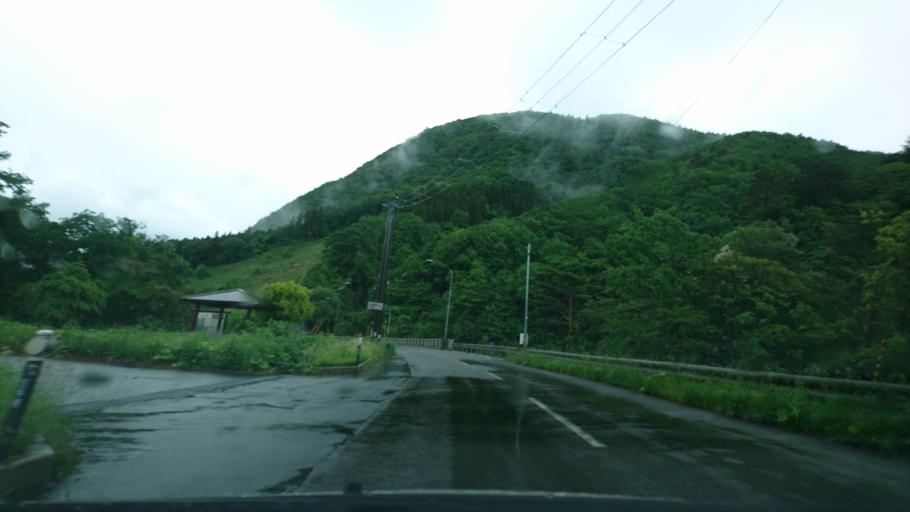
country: JP
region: Iwate
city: Ichinoseki
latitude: 38.9857
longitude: 140.9121
